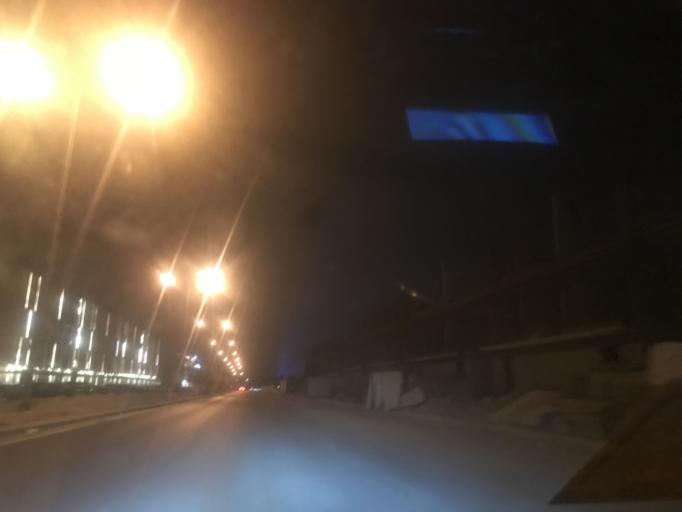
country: SA
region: Ar Riyad
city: Riyadh
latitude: 24.8022
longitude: 46.5925
